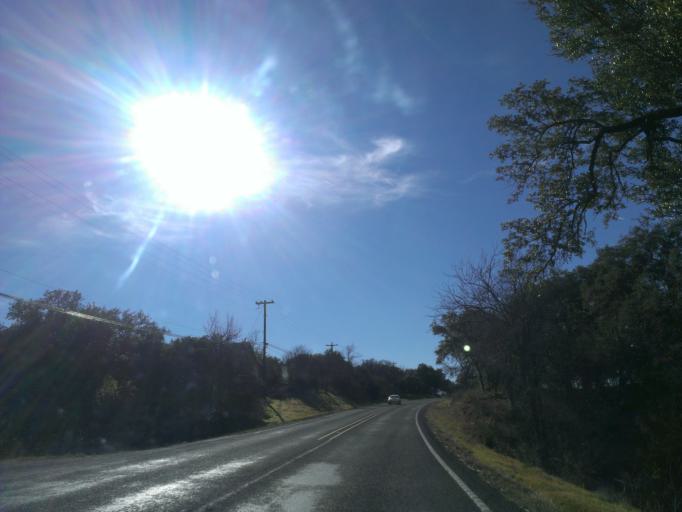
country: US
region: Texas
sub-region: Burnet County
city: Meadowlakes
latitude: 30.5471
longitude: -98.2959
